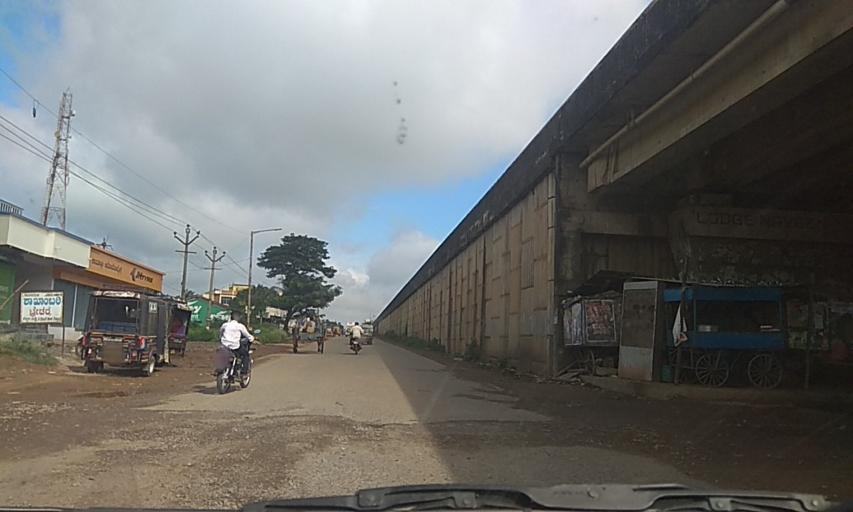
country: IN
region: Karnataka
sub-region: Haveri
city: Shiggaon
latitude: 14.9888
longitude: 75.2198
